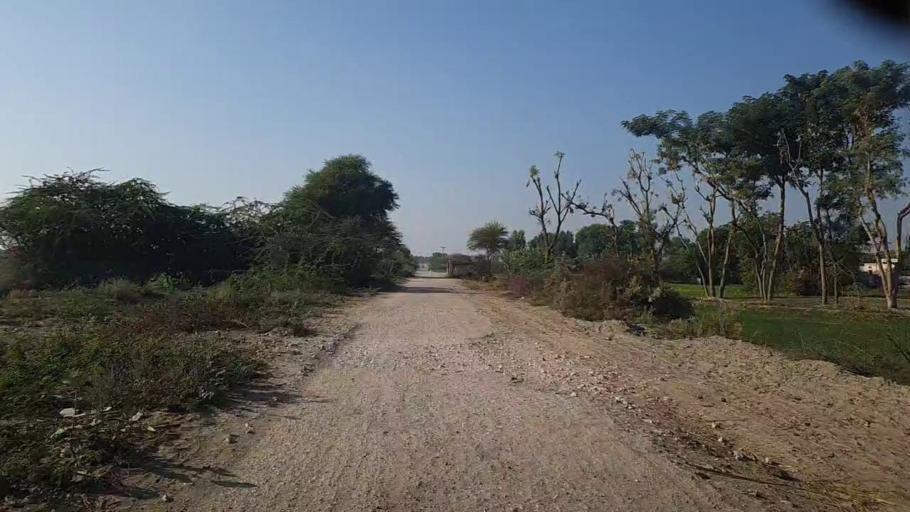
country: PK
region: Sindh
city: Darya Khan Marri
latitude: 26.6756
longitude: 68.3771
